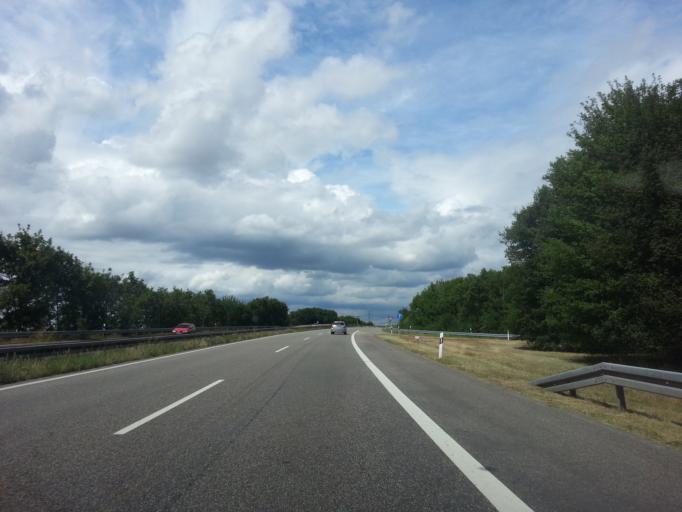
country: DE
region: Baden-Wuerttemberg
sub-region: Karlsruhe Region
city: Ketsch
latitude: 49.3548
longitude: 8.5471
